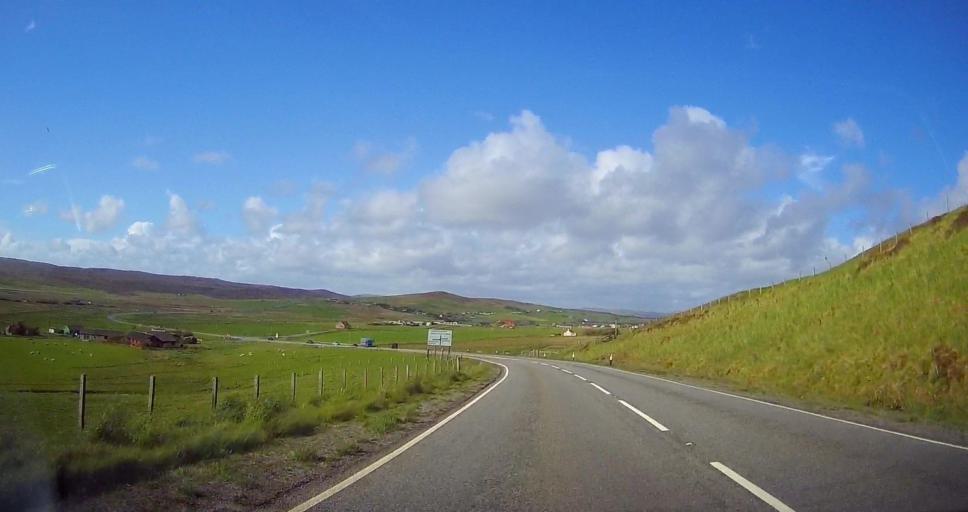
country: GB
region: Scotland
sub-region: Shetland Islands
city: Lerwick
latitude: 60.1828
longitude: -1.2248
